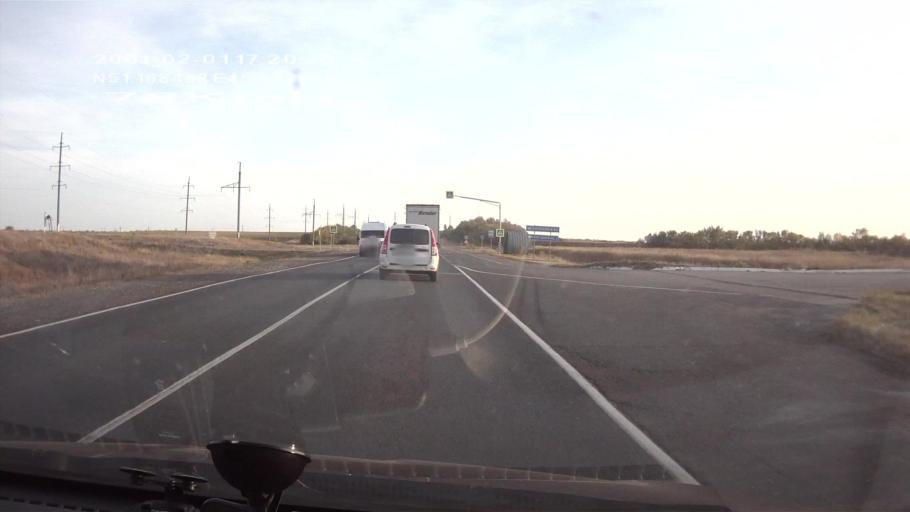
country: RU
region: Saratov
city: Krasnoarmeysk
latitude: 51.1676
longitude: 45.6489
